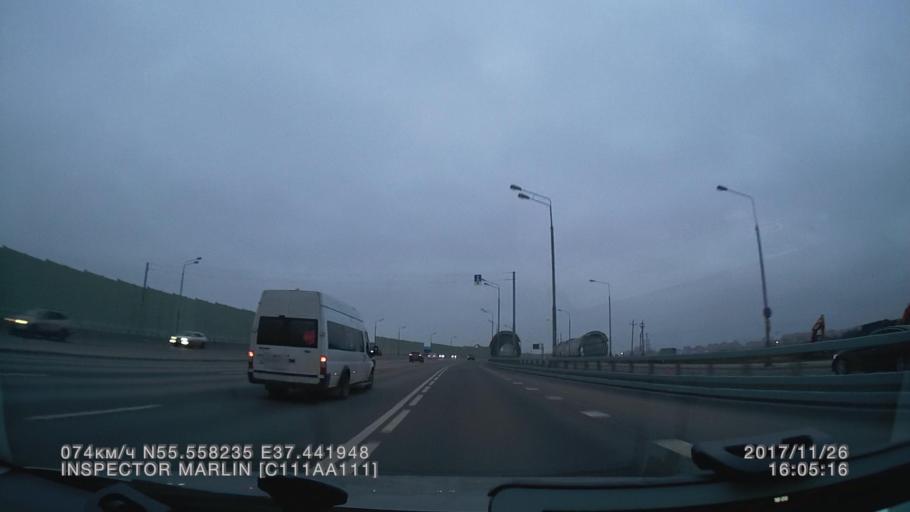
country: RU
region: Moskovskaya
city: Kommunarka
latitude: 55.5585
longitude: 37.4421
